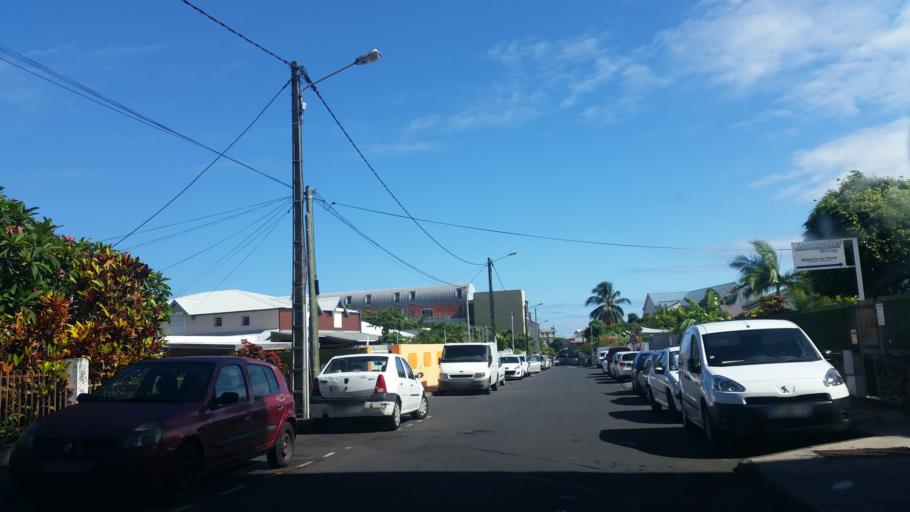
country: RE
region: Reunion
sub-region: Reunion
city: Saint-Denis
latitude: -20.8924
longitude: 55.4835
